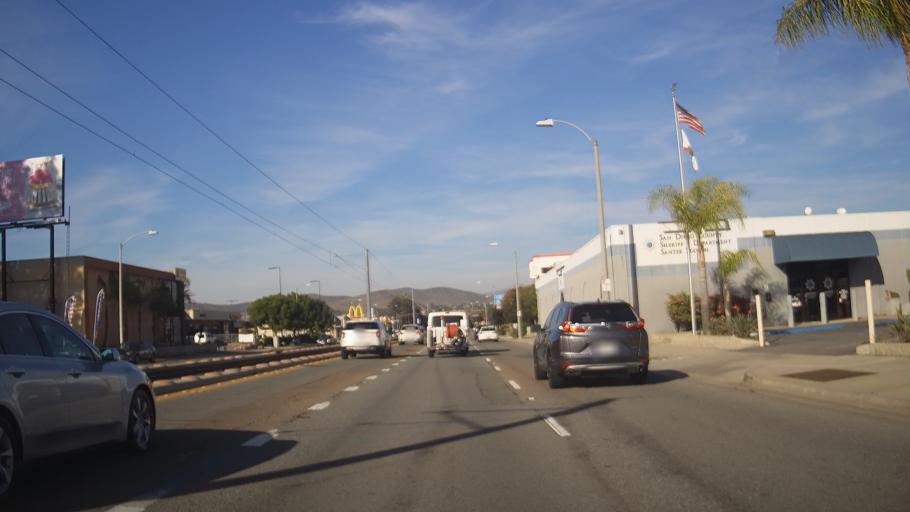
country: US
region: California
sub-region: San Diego County
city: Santee
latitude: 32.8360
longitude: -116.9837
